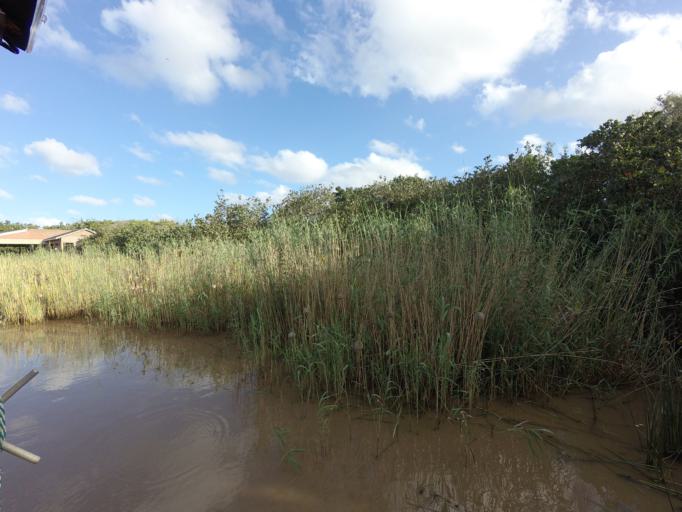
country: ZA
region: KwaZulu-Natal
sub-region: uMkhanyakude District Municipality
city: Mtubatuba
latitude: -28.3626
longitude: 32.4107
